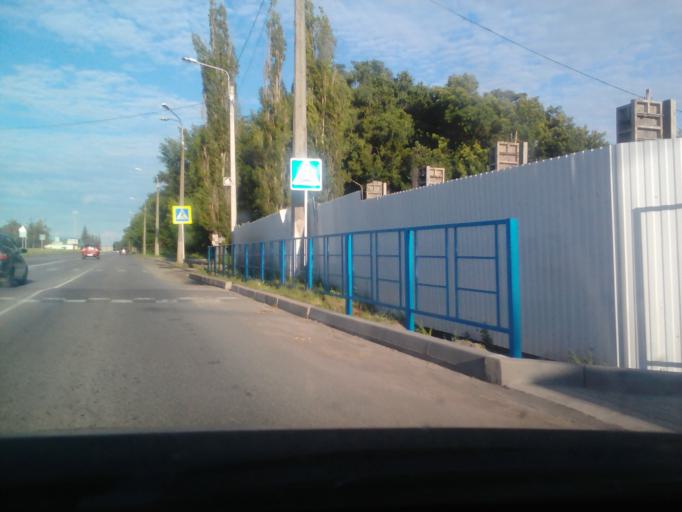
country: RU
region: Kursk
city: Kurchatov
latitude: 51.6576
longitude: 35.6503
